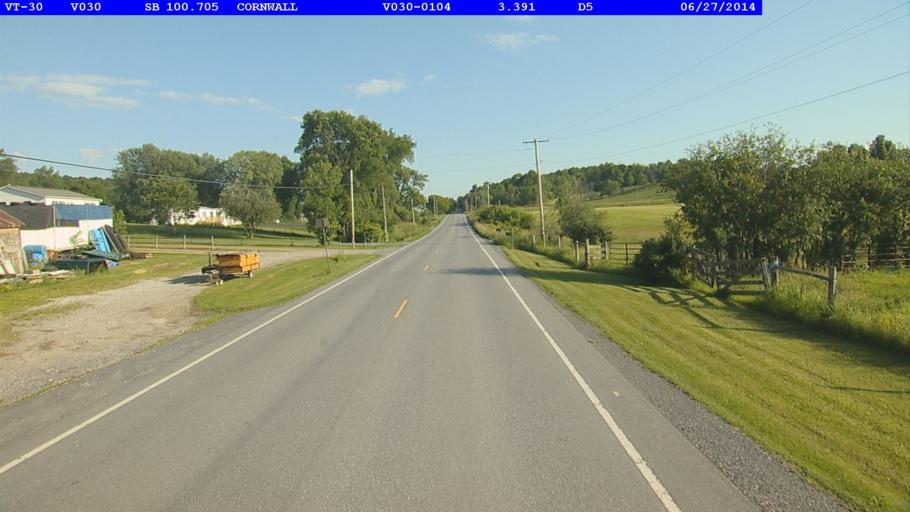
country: US
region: Vermont
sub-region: Addison County
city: Middlebury (village)
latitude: 43.9565
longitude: -73.2099
